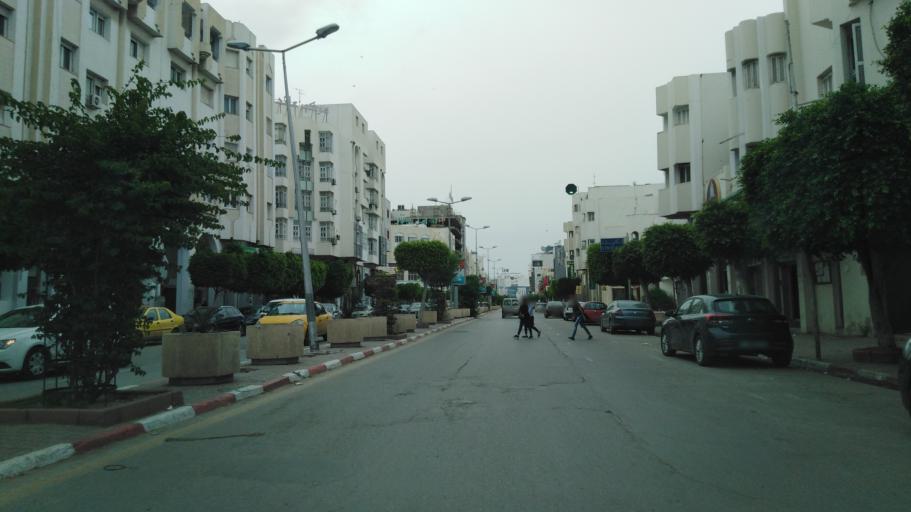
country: TN
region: Safaqis
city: Sfax
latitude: 34.7373
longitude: 10.7558
